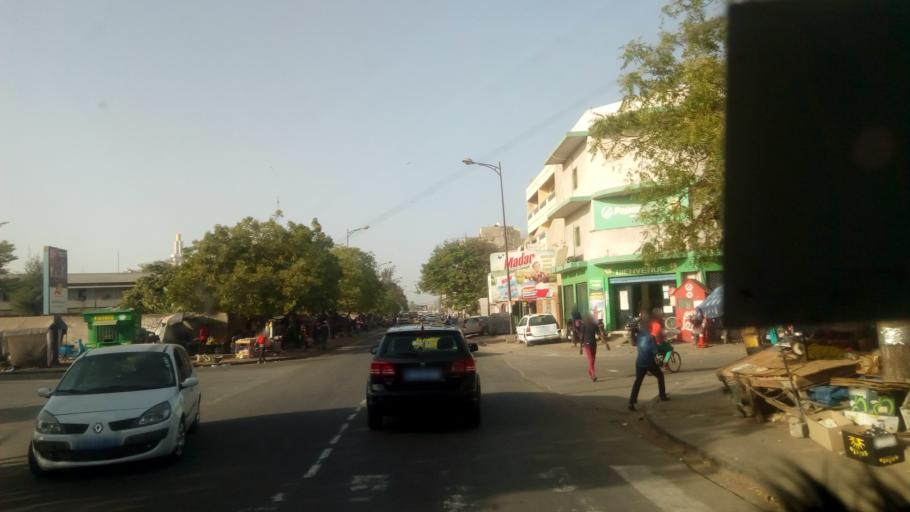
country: SN
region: Dakar
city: Dakar
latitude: 14.6955
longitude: -17.4474
